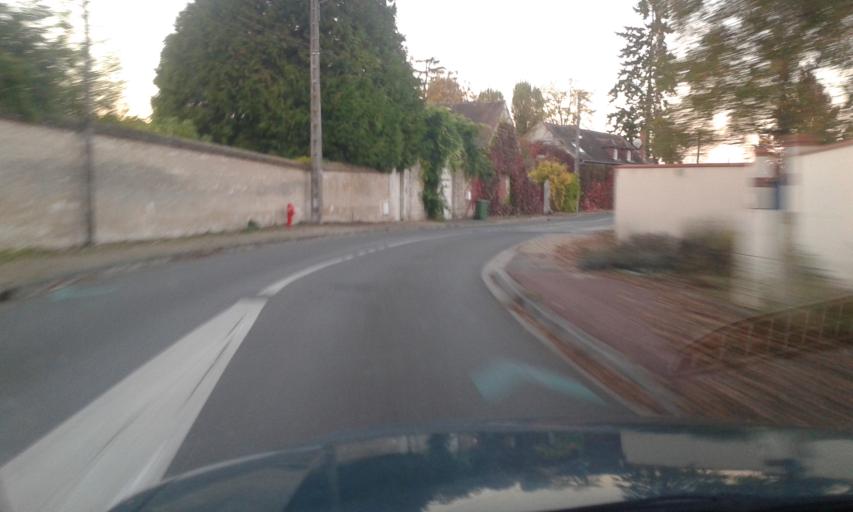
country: FR
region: Centre
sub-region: Departement du Loiret
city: Olivet
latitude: 47.8568
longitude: 1.8815
